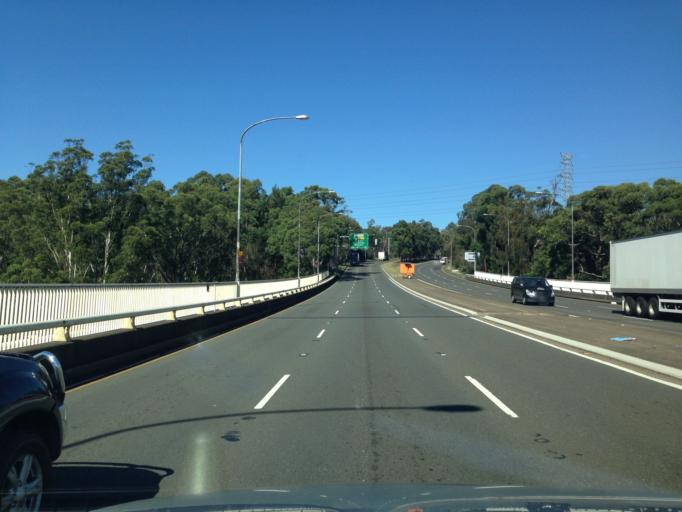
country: AU
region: New South Wales
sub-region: Ryde
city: Macquarie Park
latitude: -33.7754
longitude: 151.1356
